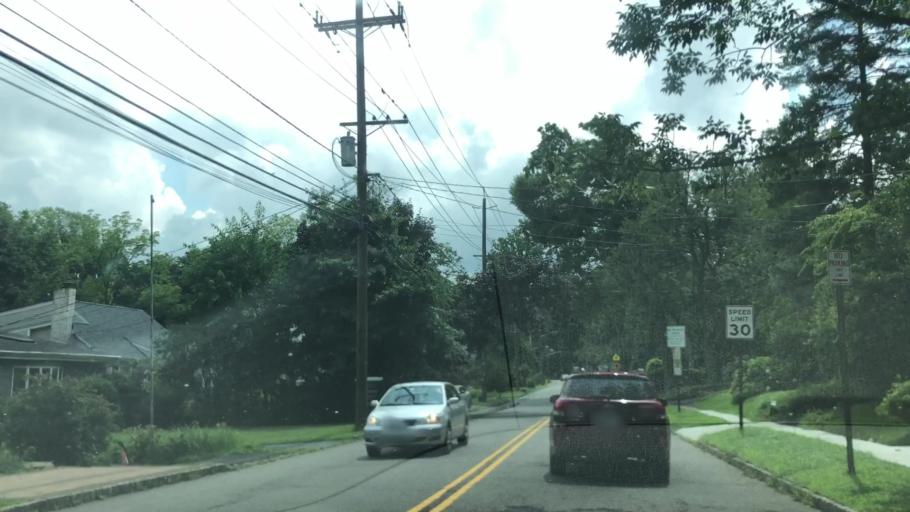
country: US
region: New Jersey
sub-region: Passaic County
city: Little Falls
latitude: 40.8600
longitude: -74.2031
